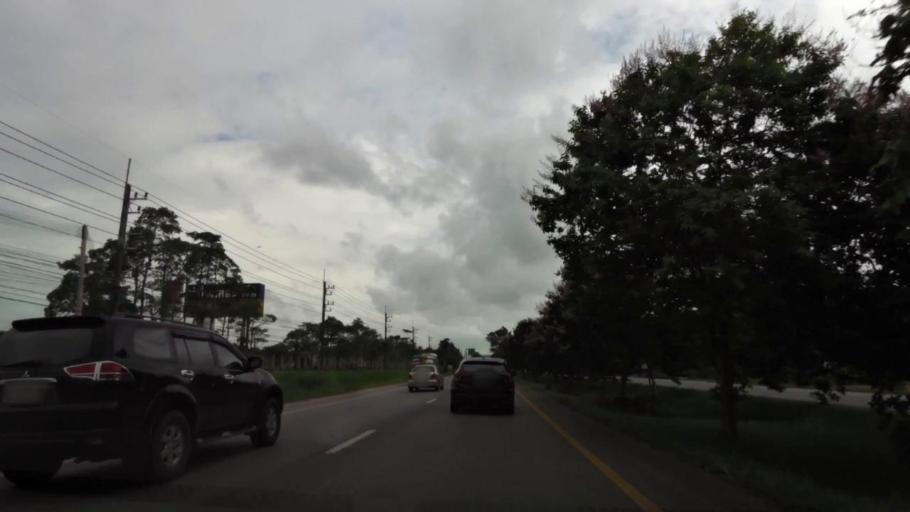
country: TH
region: Chanthaburi
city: Na Yai Am
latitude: 12.7279
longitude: 101.9250
